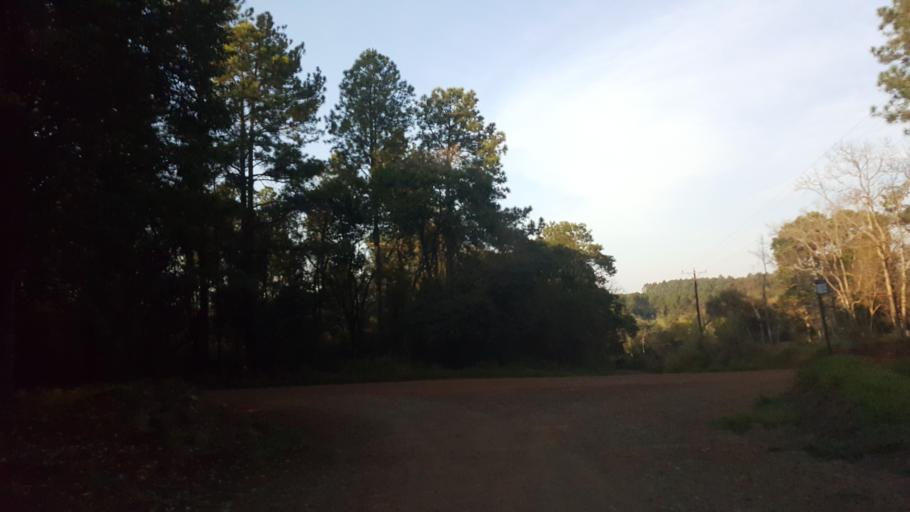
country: AR
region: Misiones
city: Capiovi
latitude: -26.8924
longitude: -55.0588
